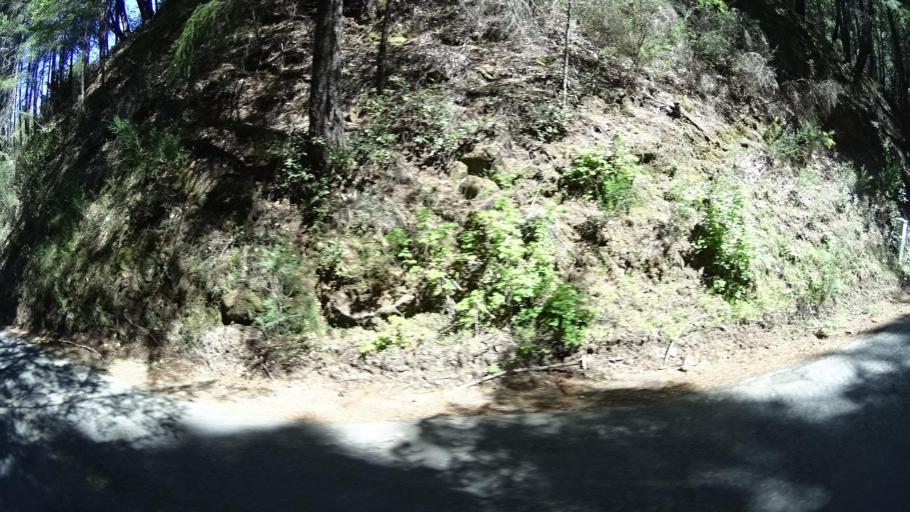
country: US
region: California
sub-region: Humboldt County
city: Redway
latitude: 40.1136
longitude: -123.9643
